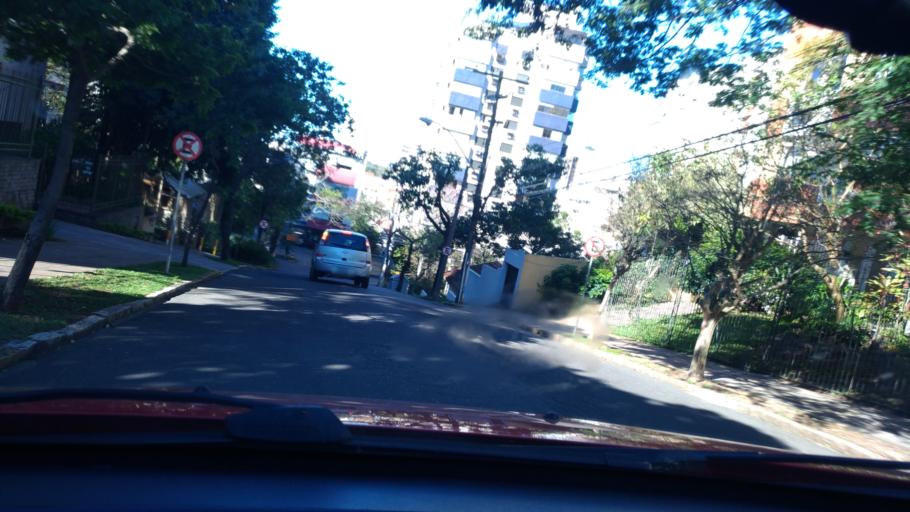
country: BR
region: Rio Grande do Sul
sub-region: Porto Alegre
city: Porto Alegre
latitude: -30.0186
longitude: -51.1848
